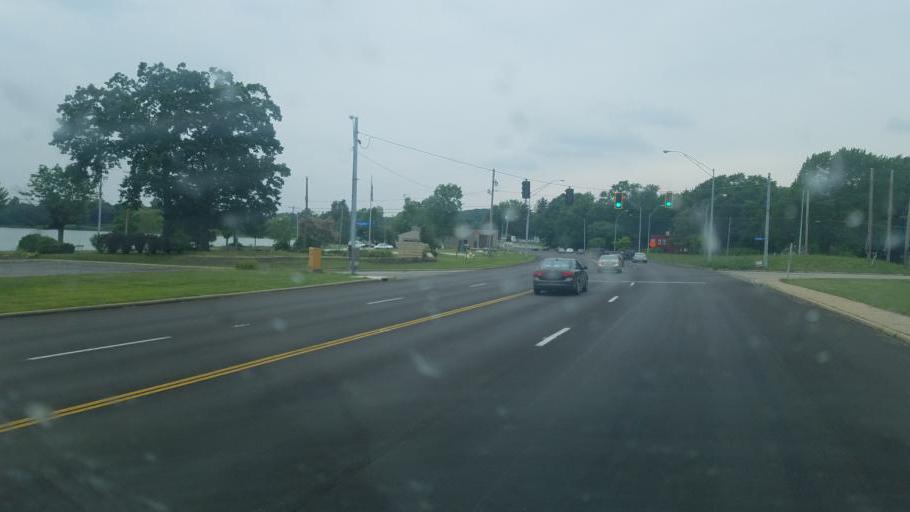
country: US
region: Ohio
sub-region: Summit County
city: Sawyerwood
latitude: 41.0350
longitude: -81.4413
